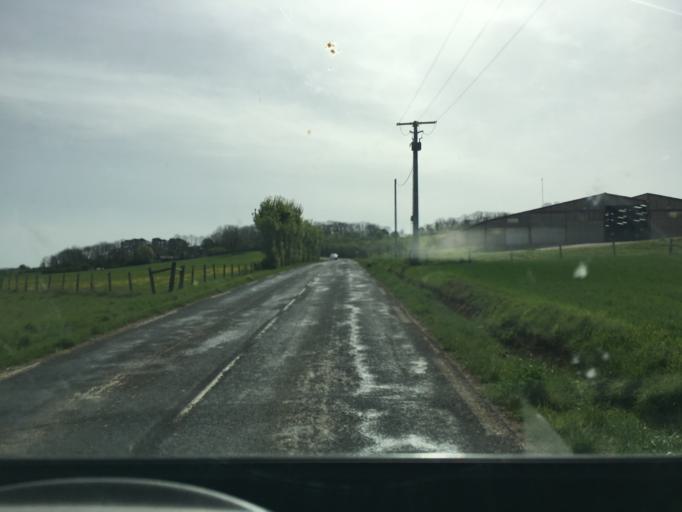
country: FR
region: Lorraine
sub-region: Departement de Meurthe-et-Moselle
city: Gondreville
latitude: 48.6615
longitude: 5.9681
